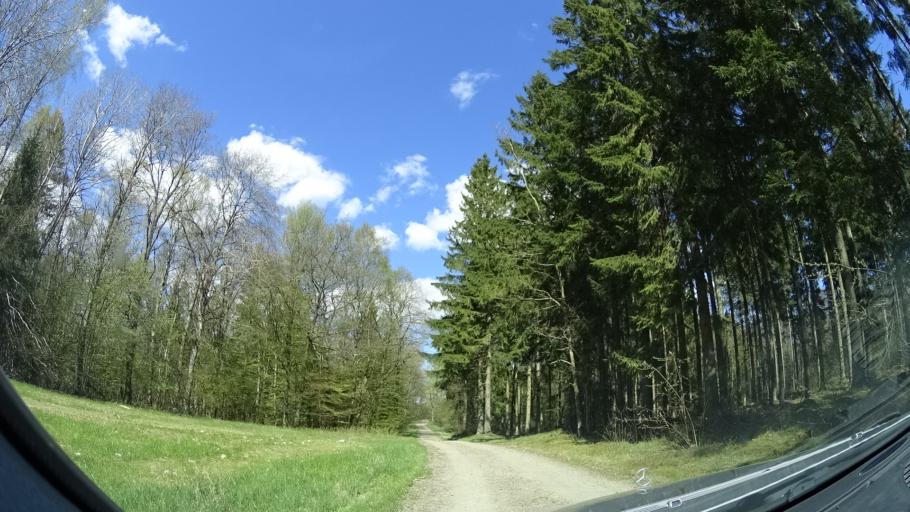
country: SE
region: Skane
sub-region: Hassleholms Kommun
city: Tormestorp
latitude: 56.0868
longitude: 13.6912
